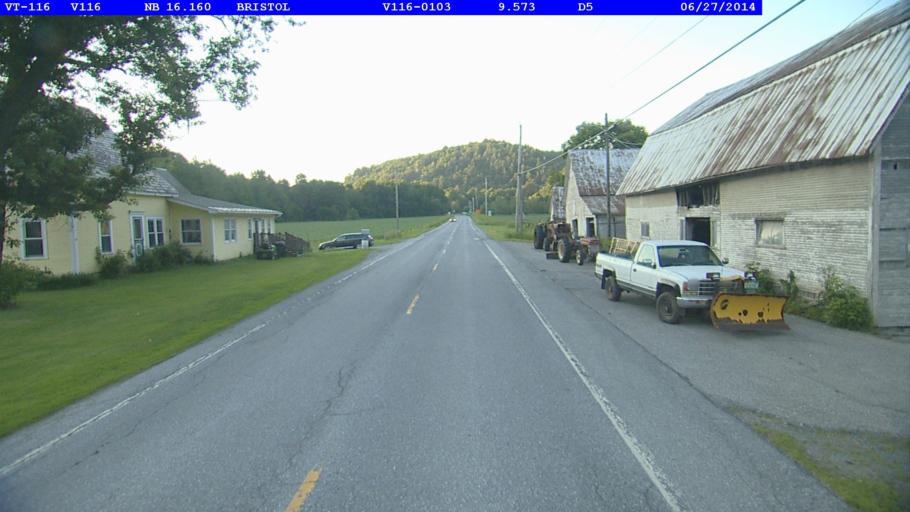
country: US
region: Vermont
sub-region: Addison County
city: Bristol
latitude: 44.1486
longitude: -73.0454
